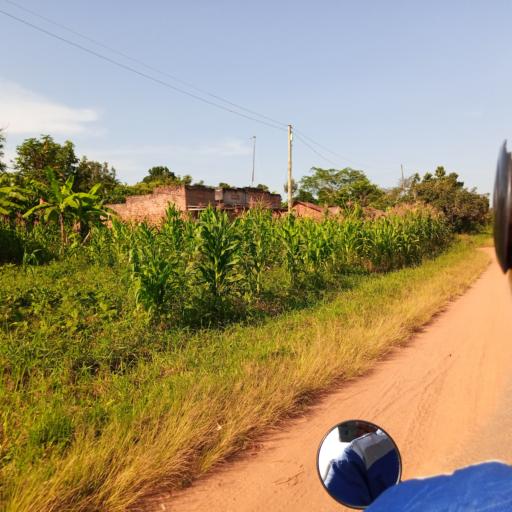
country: UG
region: Central Region
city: Masaka
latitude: -0.4275
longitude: 31.6676
